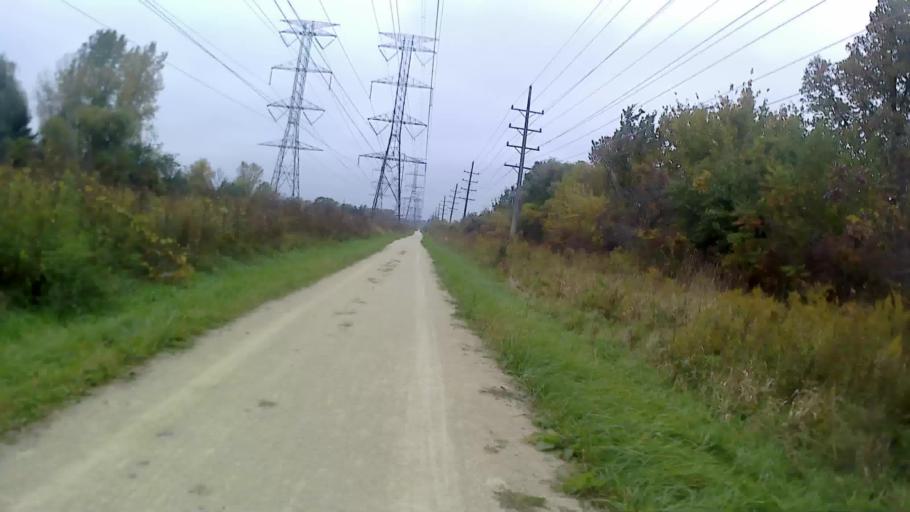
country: US
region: Illinois
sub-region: Kane County
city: Aurora
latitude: 41.7925
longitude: -88.2608
